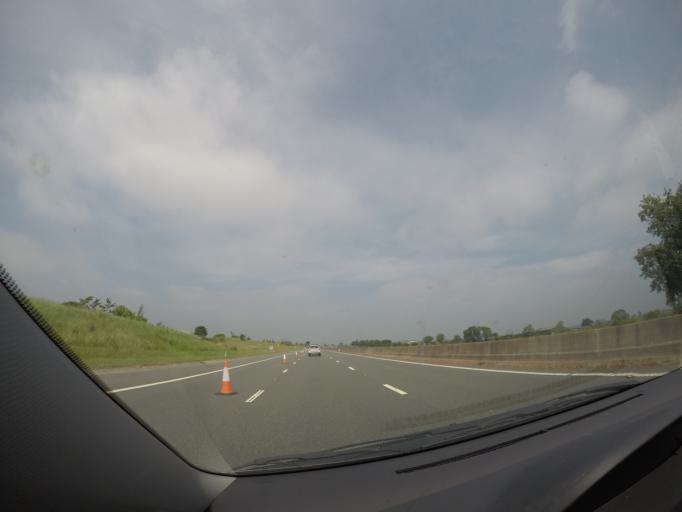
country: GB
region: England
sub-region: North Yorkshire
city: Ripon
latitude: 54.2123
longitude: -1.4787
